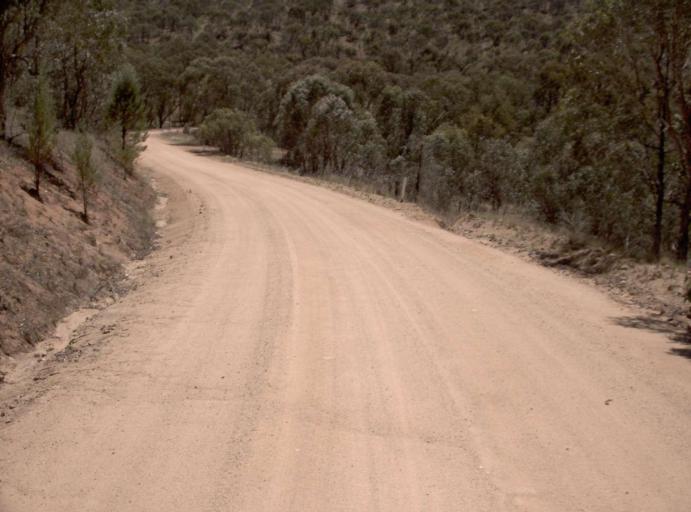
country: AU
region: New South Wales
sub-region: Snowy River
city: Jindabyne
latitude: -36.9222
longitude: 148.3922
